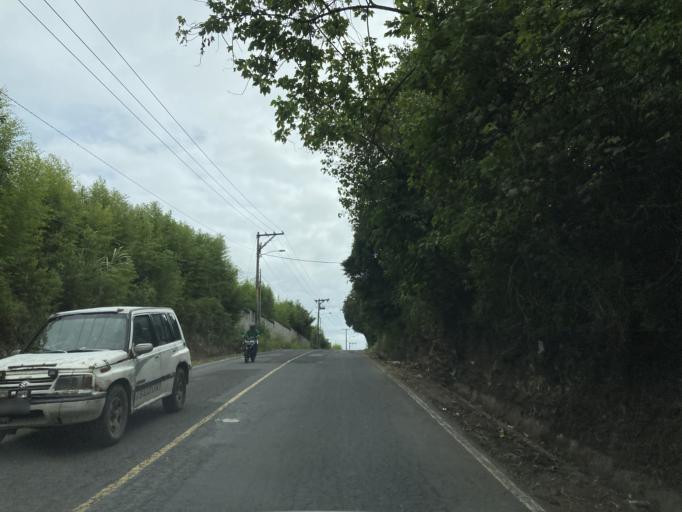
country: GT
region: Guatemala
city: San Jose Pinula
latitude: 14.5265
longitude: -90.4113
